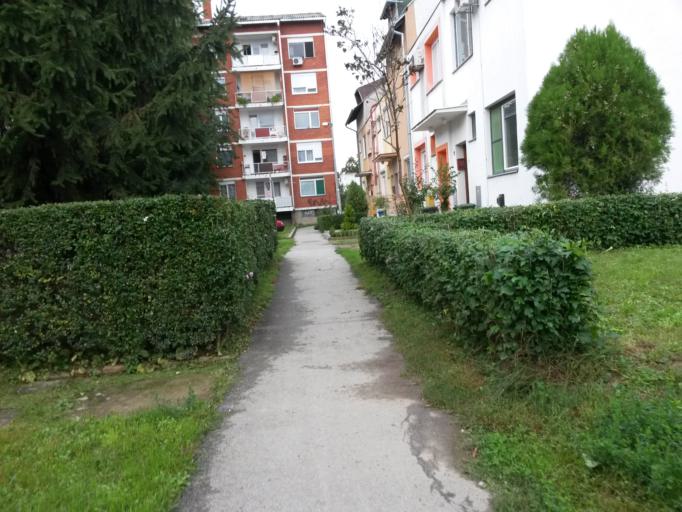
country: HR
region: Osjecko-Baranjska
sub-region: Grad Osijek
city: Osijek
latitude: 45.5440
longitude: 18.7142
